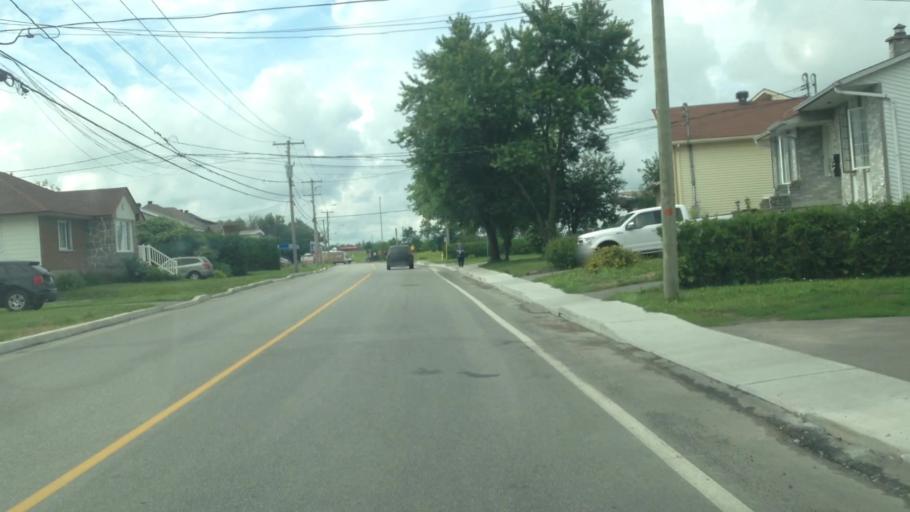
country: CA
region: Quebec
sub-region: Laurentides
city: Blainville
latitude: 45.6979
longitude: -73.9356
